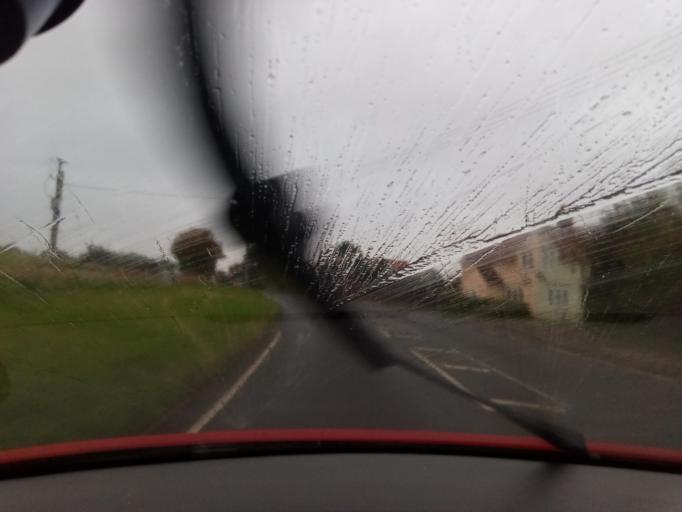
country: GB
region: England
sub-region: Suffolk
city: Kedington
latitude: 52.0654
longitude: 0.4820
